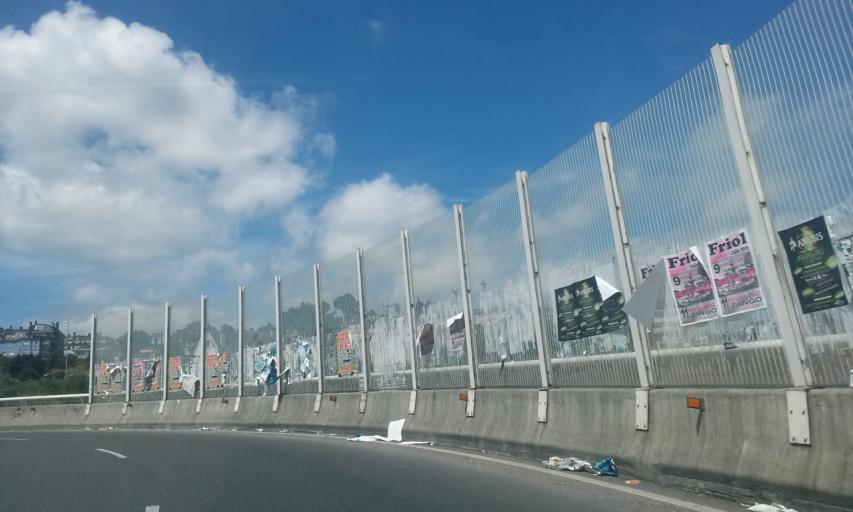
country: ES
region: Galicia
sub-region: Provincia de Lugo
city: Lugo
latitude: 42.9966
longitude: -7.5635
